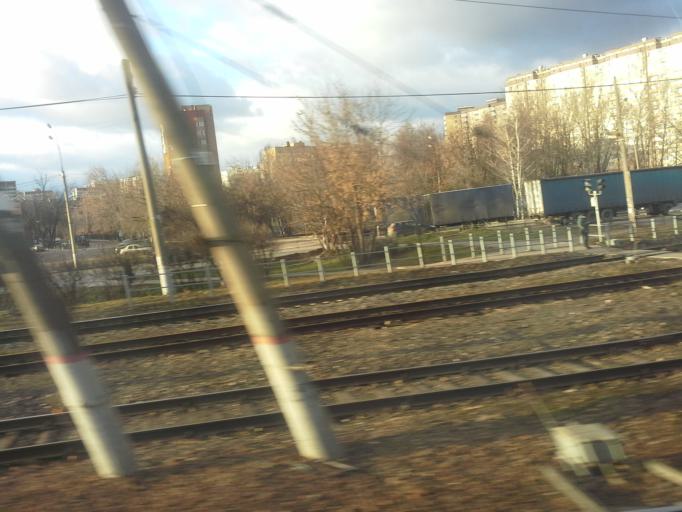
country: RU
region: Moskovskaya
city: Mytishchi
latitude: 55.9233
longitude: 37.7715
